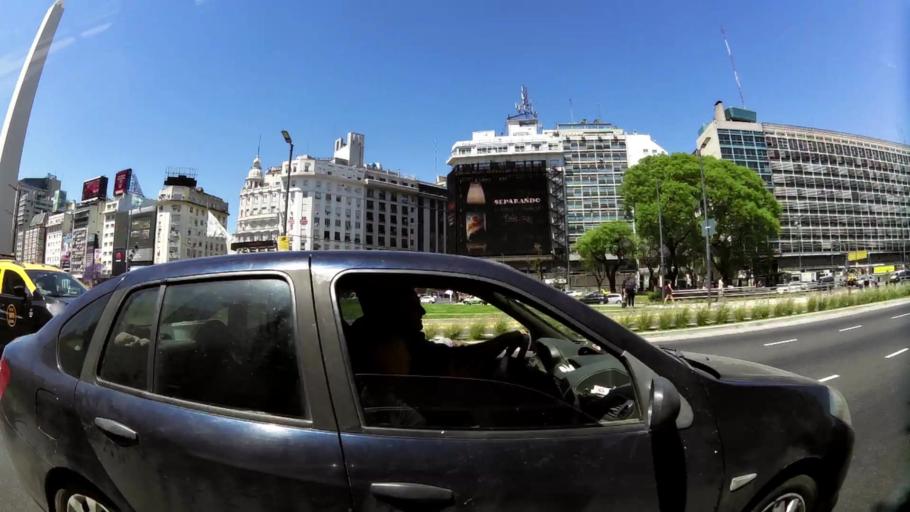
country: AR
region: Buenos Aires F.D.
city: Buenos Aires
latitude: -34.6046
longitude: -58.3820
